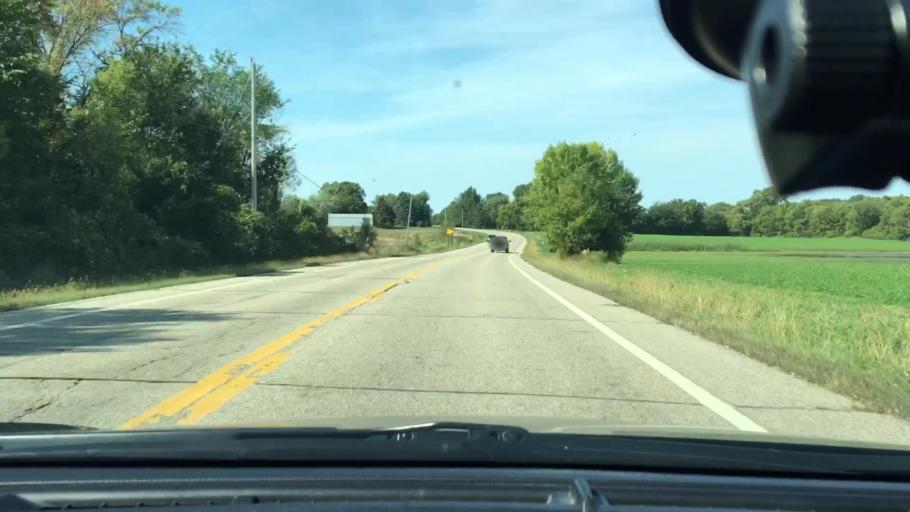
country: US
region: Minnesota
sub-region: Wright County
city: Hanover
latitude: 45.1215
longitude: -93.6098
